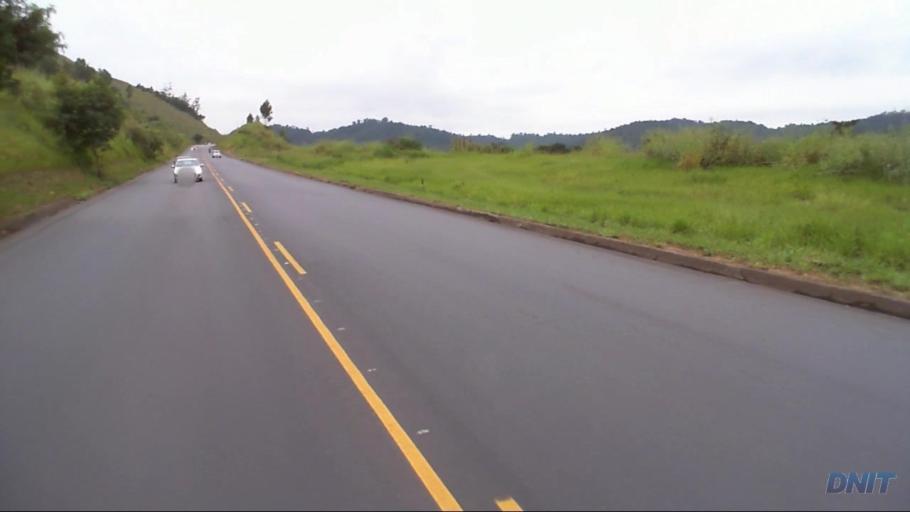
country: BR
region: Minas Gerais
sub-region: Coronel Fabriciano
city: Coronel Fabriciano
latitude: -19.5341
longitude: -42.5880
